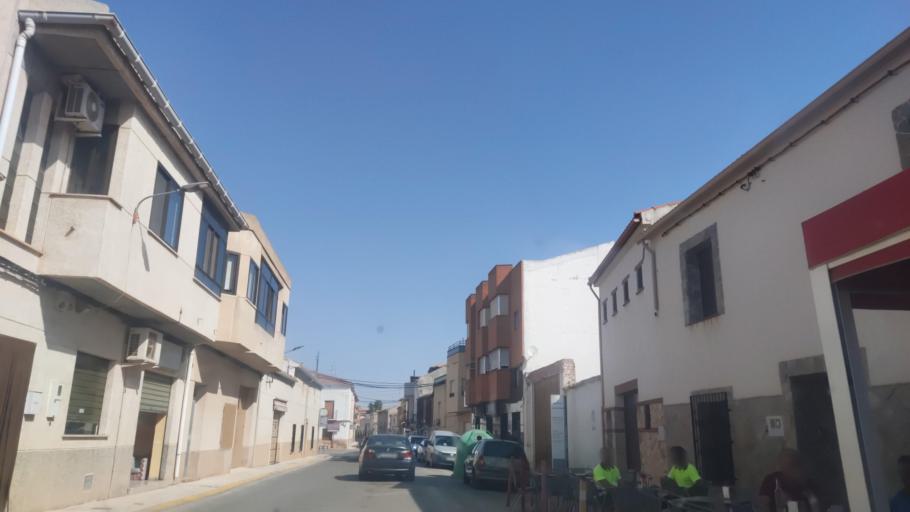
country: ES
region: Castille-La Mancha
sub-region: Provincia de Albacete
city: La Gineta
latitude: 39.1132
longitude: -1.9963
